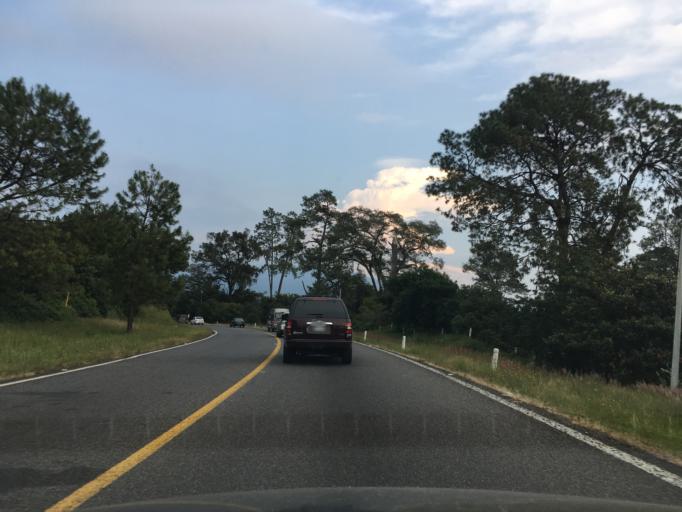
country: MX
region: Michoacan
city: Tingambato
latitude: 19.4751
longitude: -101.9059
